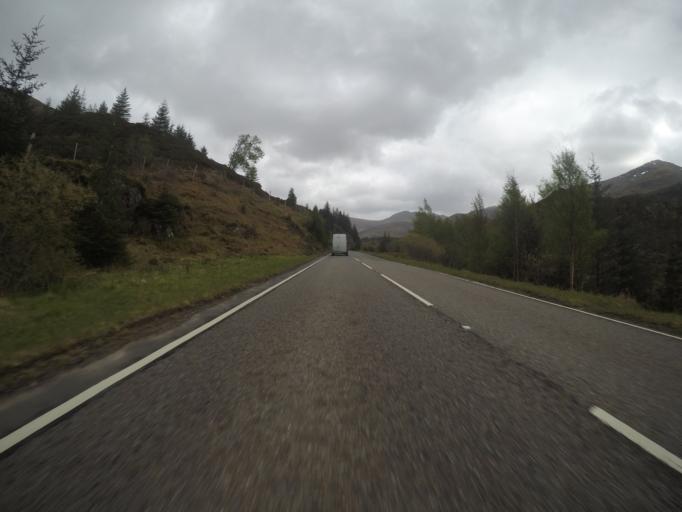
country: GB
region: Scotland
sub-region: Highland
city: Fort William
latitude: 57.1633
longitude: -5.2716
